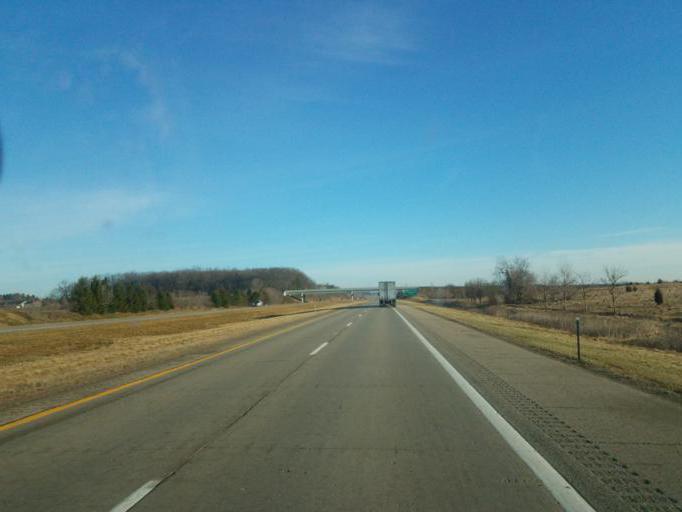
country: US
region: Michigan
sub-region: Clinton County
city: DeWitt
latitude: 42.8389
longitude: -84.5185
